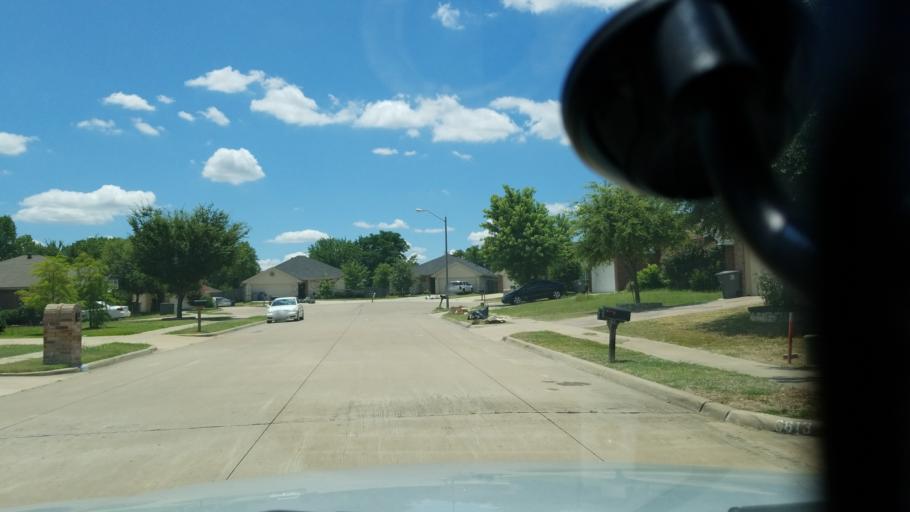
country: US
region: Texas
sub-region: Dallas County
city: Duncanville
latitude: 32.6666
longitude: -96.8791
